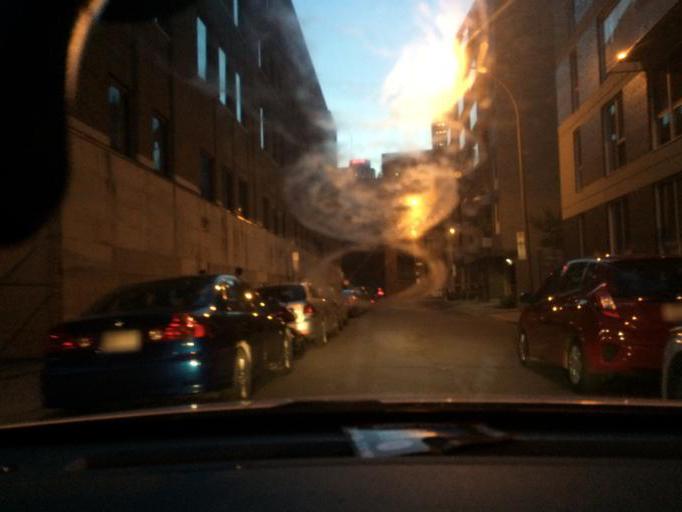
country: CA
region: Quebec
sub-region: Montreal
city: Montreal
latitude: 45.4950
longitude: -73.5600
